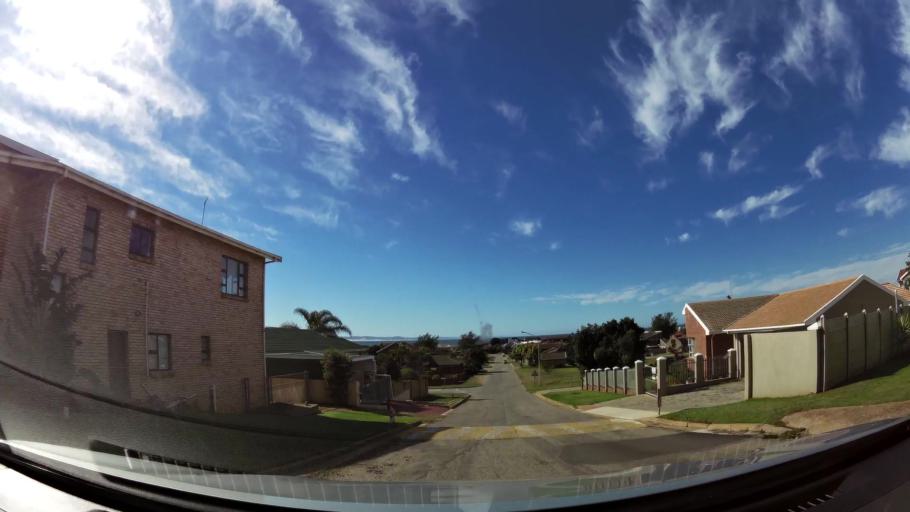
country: ZA
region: Eastern Cape
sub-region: Cacadu District Municipality
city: Jeffrey's Bay
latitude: -34.0185
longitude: 24.9244
